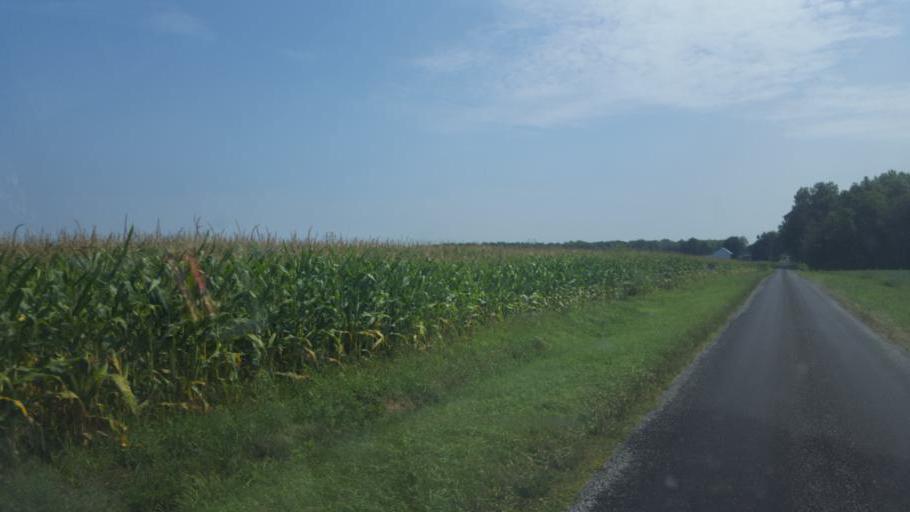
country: US
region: Ohio
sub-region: Delaware County
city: Ashley
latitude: 40.4987
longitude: -83.0122
